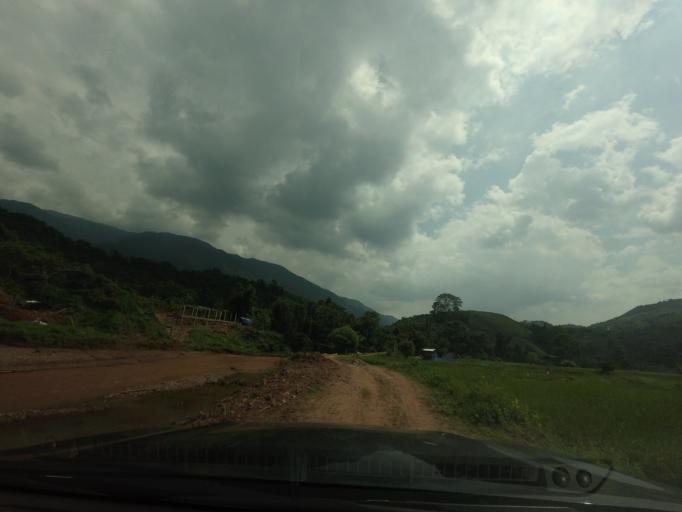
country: TH
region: Nan
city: Bo Kluea
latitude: 19.1932
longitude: 101.2038
